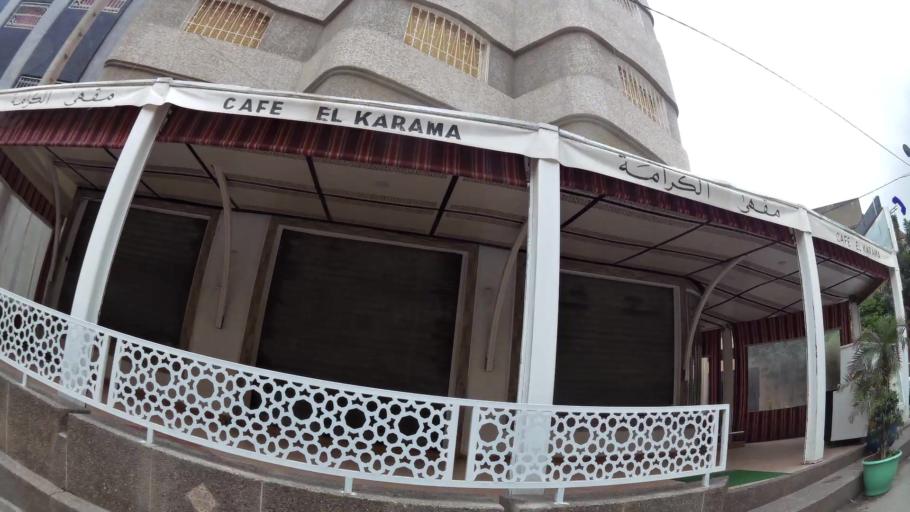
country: MA
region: Rabat-Sale-Zemmour-Zaer
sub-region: Khemisset
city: Tiflet
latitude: 33.8889
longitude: -6.3176
